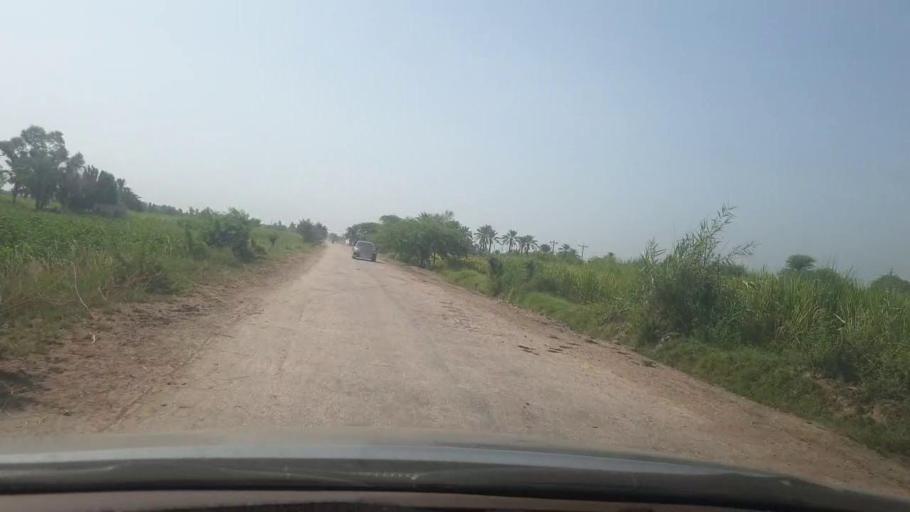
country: PK
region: Sindh
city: Gambat
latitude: 27.3084
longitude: 68.5640
